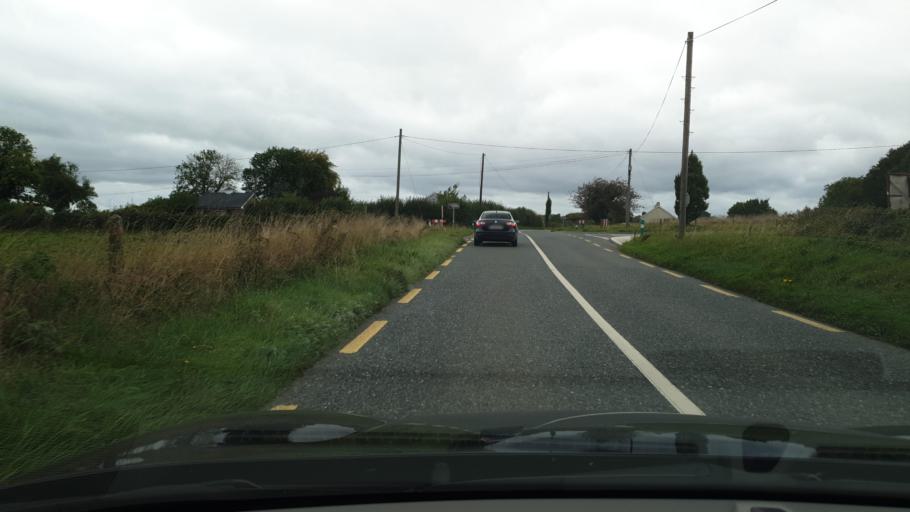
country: IE
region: Leinster
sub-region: Kildare
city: Clane
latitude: 53.2772
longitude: -6.6952
